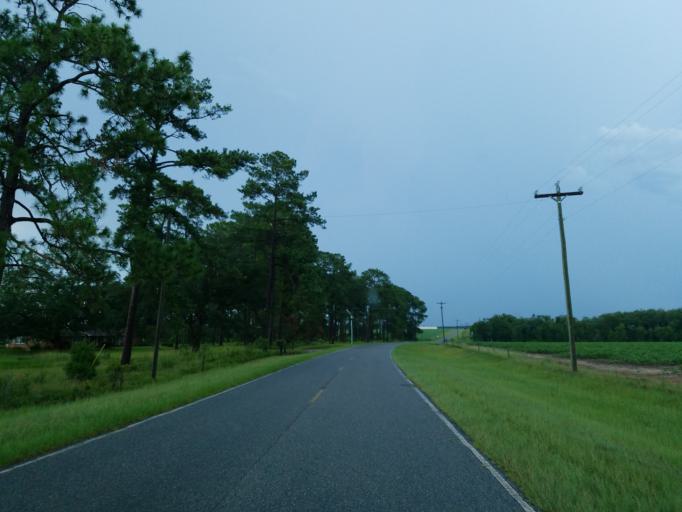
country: US
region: Georgia
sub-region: Cook County
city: Adel
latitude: 31.0736
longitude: -83.4380
